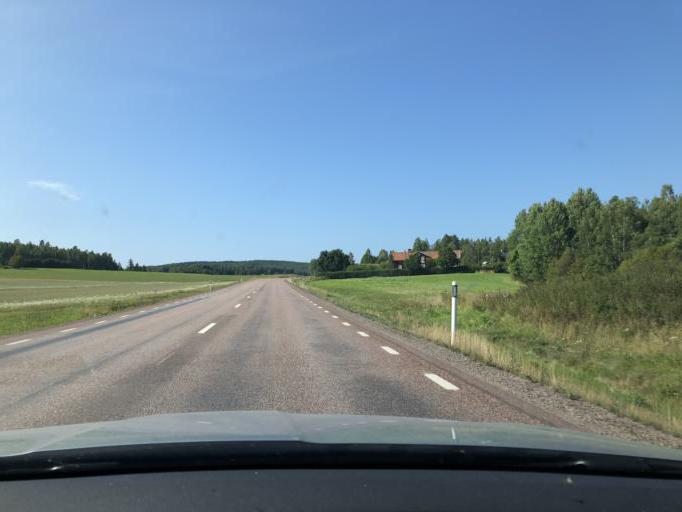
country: SE
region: Dalarna
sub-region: Saters Kommun
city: Saeter
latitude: 60.4397
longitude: 15.8179
